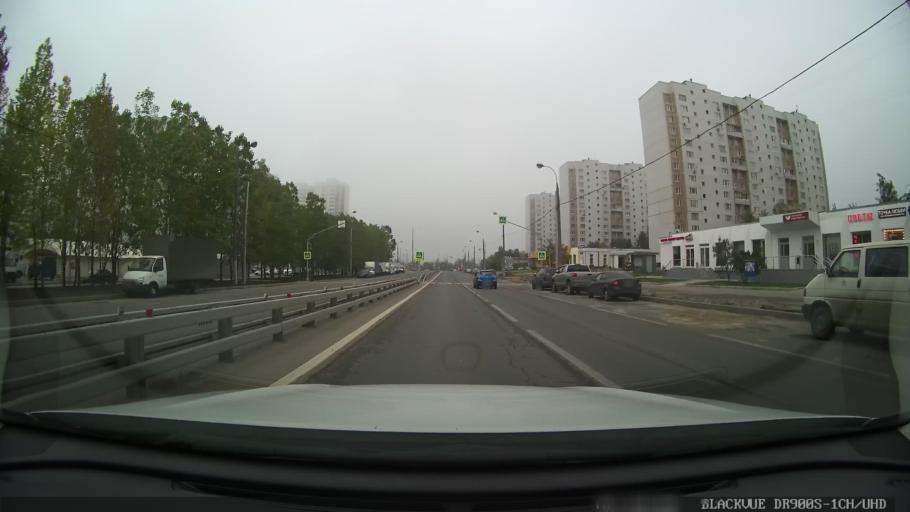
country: RU
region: Moscow
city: Solntsevo
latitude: 55.6417
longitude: 37.3642
